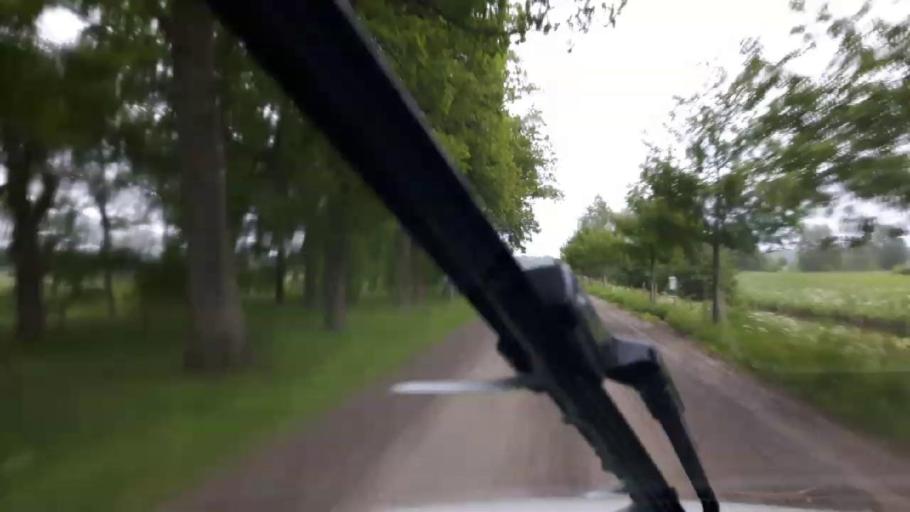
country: SE
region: Vaestmanland
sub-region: Arboga Kommun
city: Tyringe
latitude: 59.3923
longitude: 15.9275
